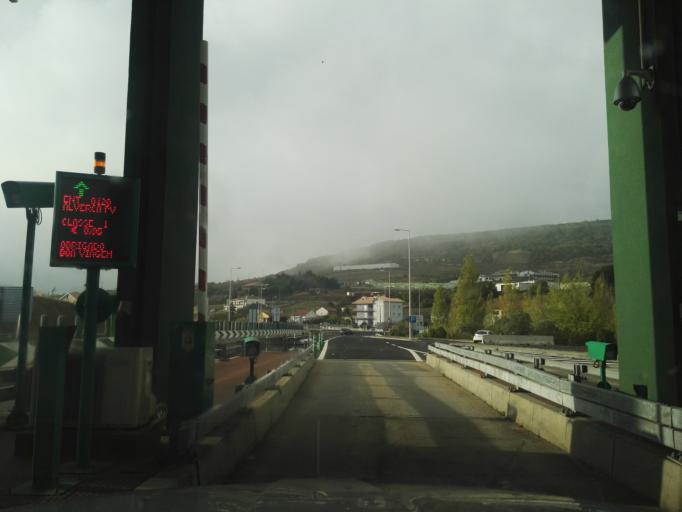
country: PT
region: Lisbon
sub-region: Arruda Dos Vinhos
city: Arruda dos Vinhos
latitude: 38.9647
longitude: -9.0607
